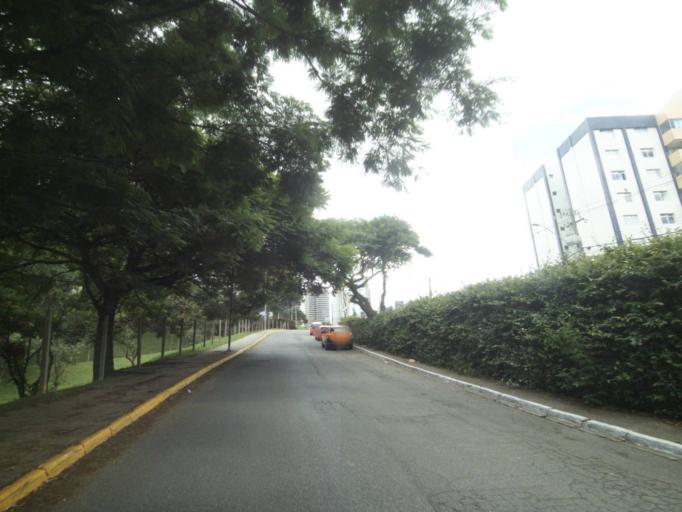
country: BR
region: Parana
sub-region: Curitiba
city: Curitiba
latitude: -25.4371
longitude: -49.3199
